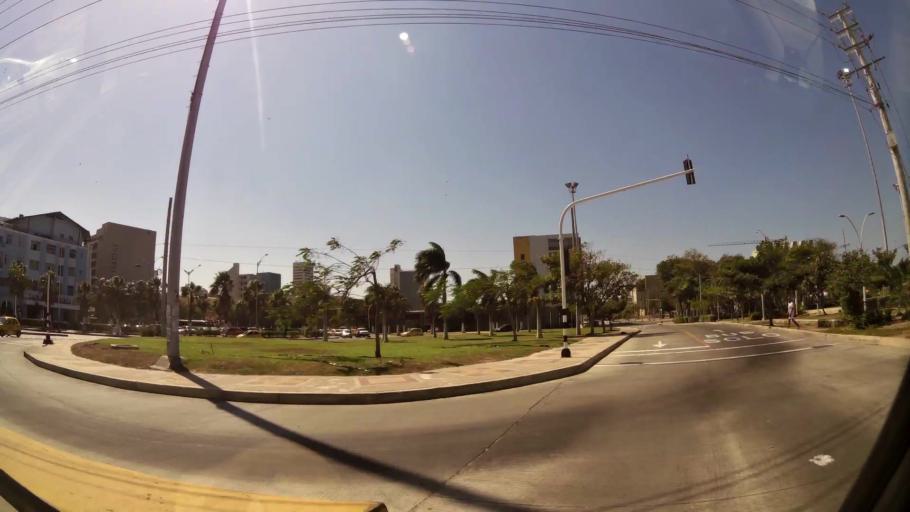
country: CO
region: Atlantico
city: Barranquilla
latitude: 10.9855
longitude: -74.7760
